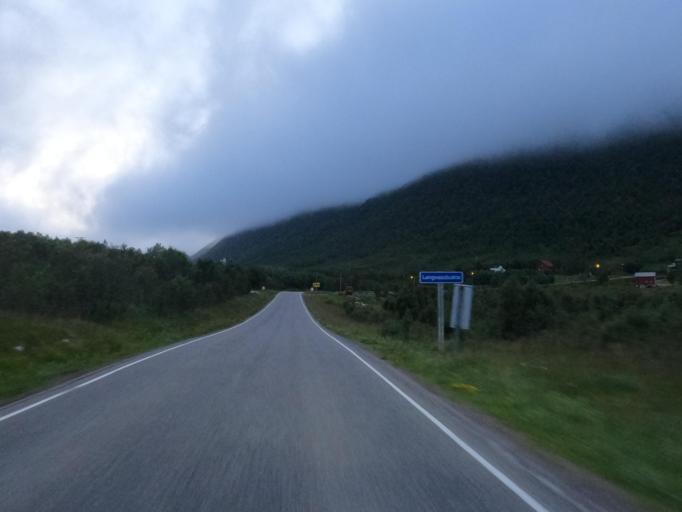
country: NO
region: Nordland
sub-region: Lodingen
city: Lodingen
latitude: 68.6146
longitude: 15.7653
